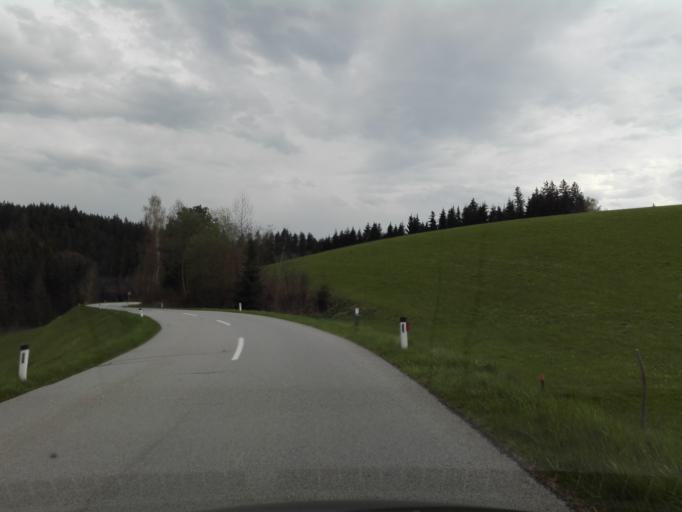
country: AT
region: Upper Austria
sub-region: Politischer Bezirk Rohrbach
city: Atzesberg
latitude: 48.5437
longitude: 13.9520
